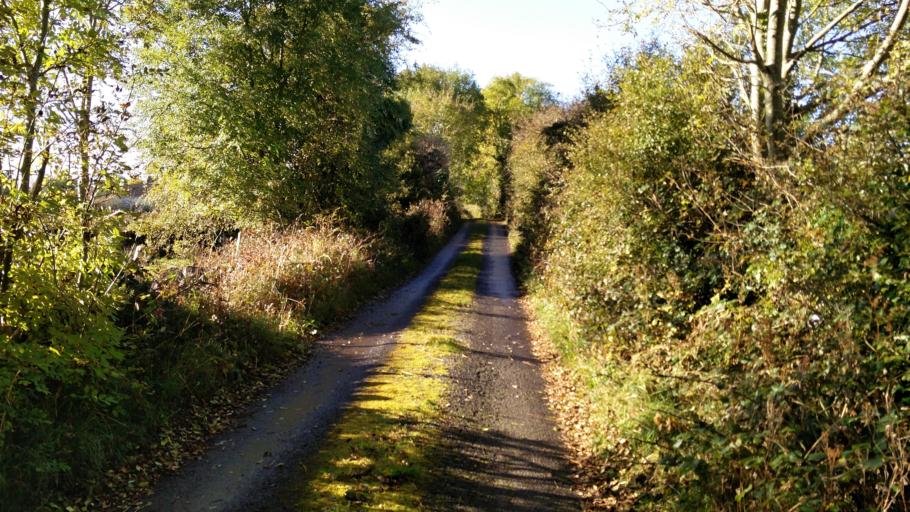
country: IE
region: Connaught
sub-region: Maigh Eo
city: Westport
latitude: 53.7799
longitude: -9.4408
